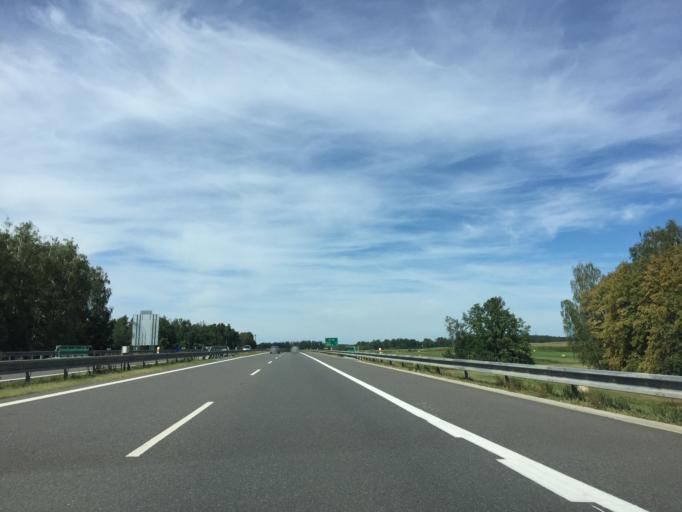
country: CZ
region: Jihocesky
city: Sobeslav
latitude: 49.2290
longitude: 14.7281
